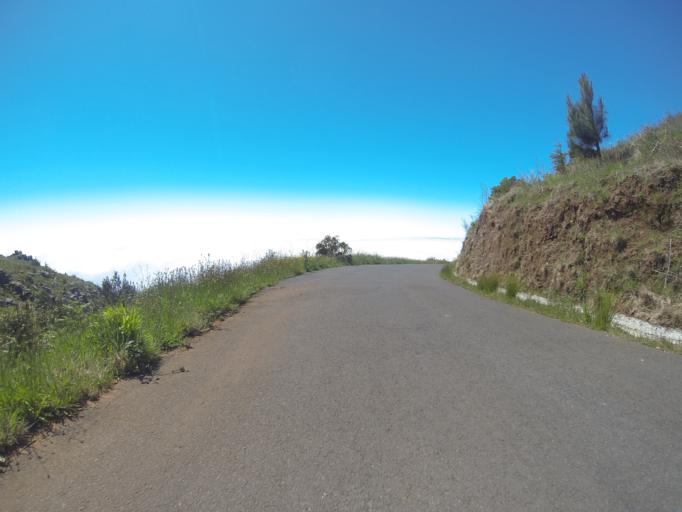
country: PT
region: Madeira
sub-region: Funchal
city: Nossa Senhora do Monte
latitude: 32.7042
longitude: -16.9122
